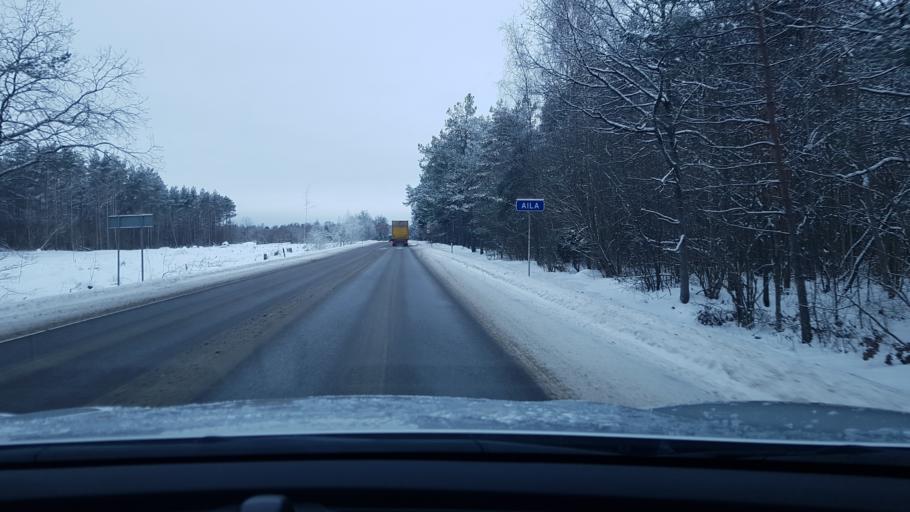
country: EE
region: Harju
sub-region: Saue linn
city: Saue
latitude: 59.3128
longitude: 24.5416
